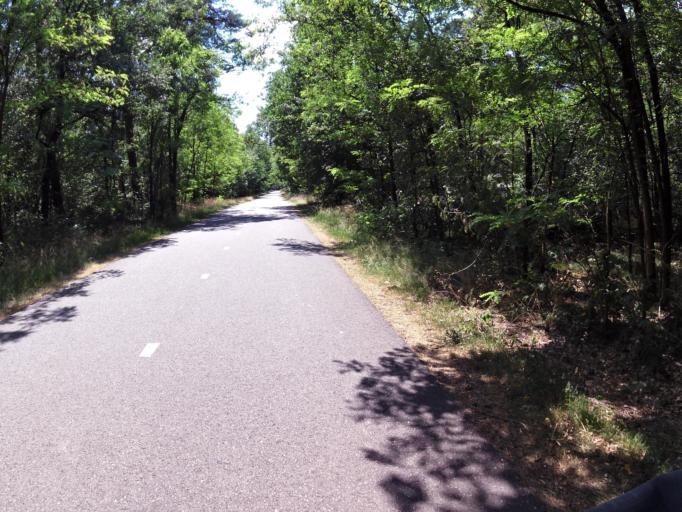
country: NL
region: North Brabant
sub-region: Gemeente Oisterwijk
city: Oisterwijk
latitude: 51.5597
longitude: 5.1987
